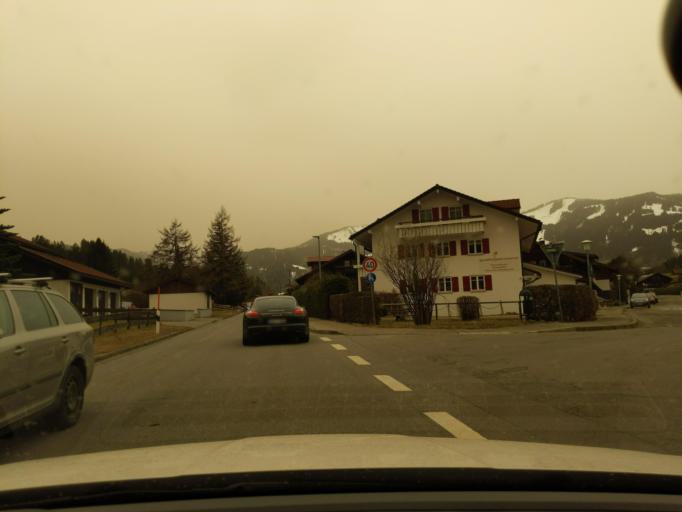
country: DE
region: Bavaria
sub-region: Swabia
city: Bolsterlang
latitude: 47.4602
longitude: 10.2653
